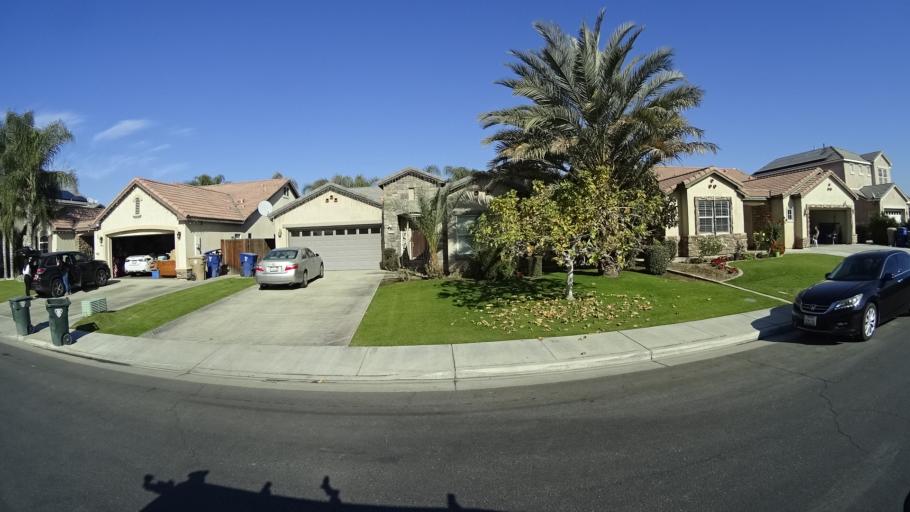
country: US
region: California
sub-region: Kern County
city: Greenfield
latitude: 35.2721
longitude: -119.0600
